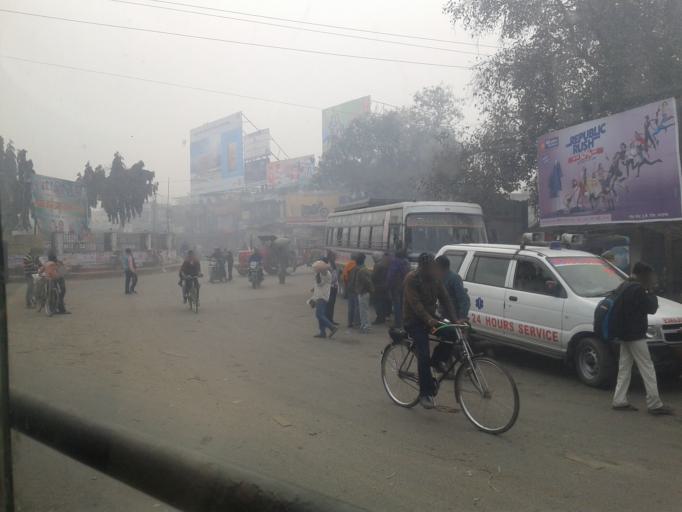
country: IN
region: Bihar
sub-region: Muzaffarpur
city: Muzaffarpur
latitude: 26.1489
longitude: 85.3898
